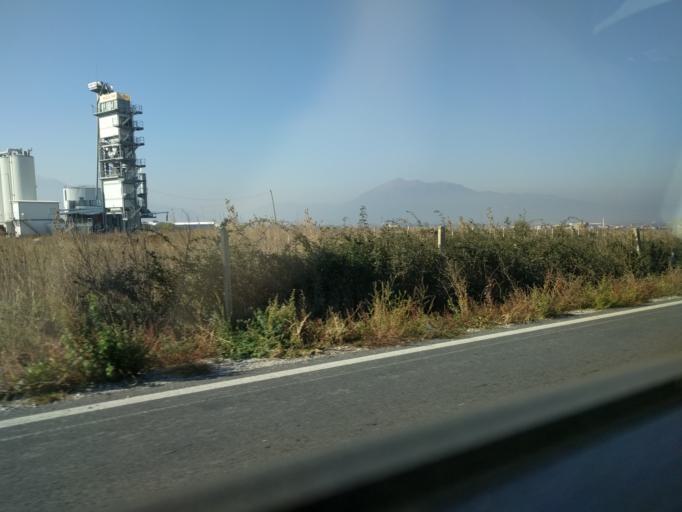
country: XK
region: Prizren
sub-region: Prizren
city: Prizren
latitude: 42.2381
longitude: 20.7575
